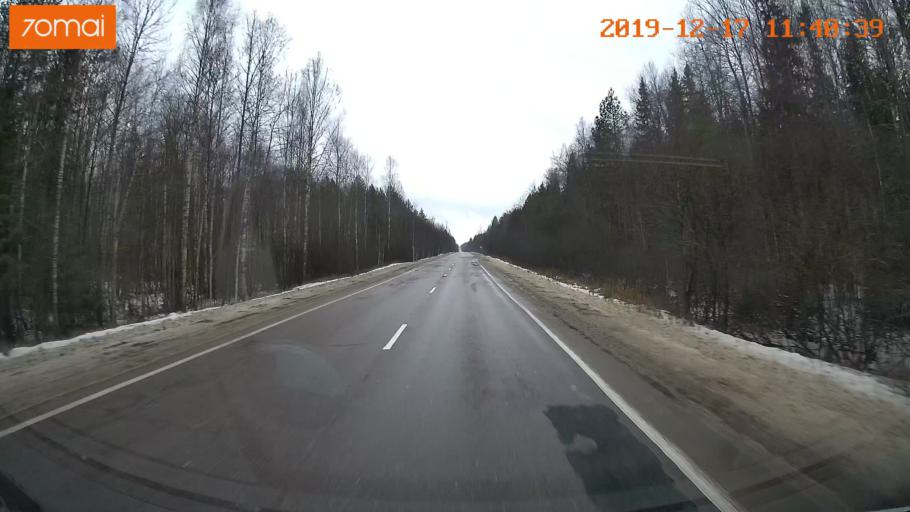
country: RU
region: Vladimir
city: Velikodvorskiy
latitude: 55.3144
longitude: 40.6737
